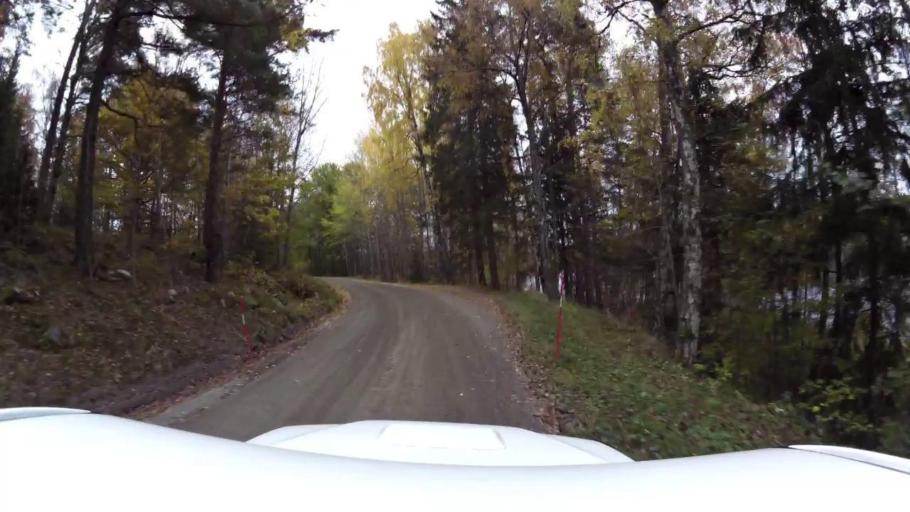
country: SE
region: OEstergoetland
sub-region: Linkopings Kommun
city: Ljungsbro
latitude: 58.5765
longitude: 15.4358
